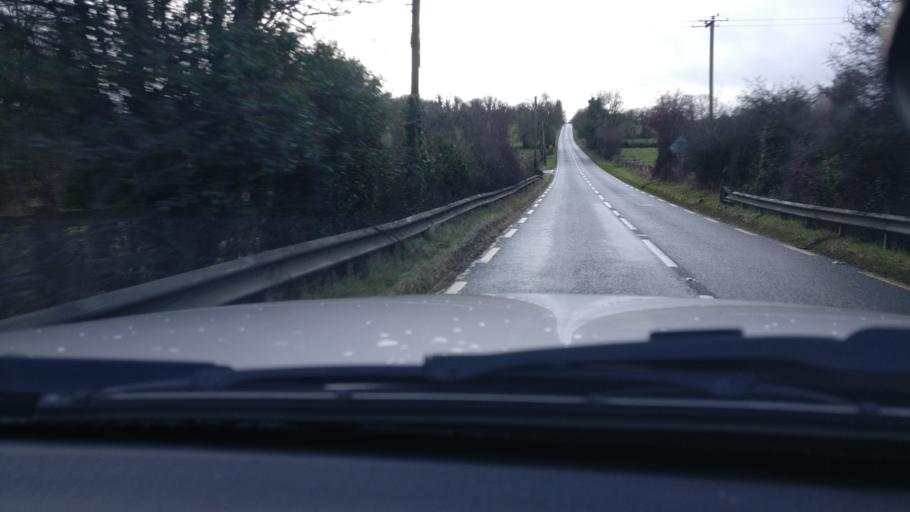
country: IE
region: Leinster
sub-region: An Iarmhi
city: Moate
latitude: 53.6226
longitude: -7.6988
